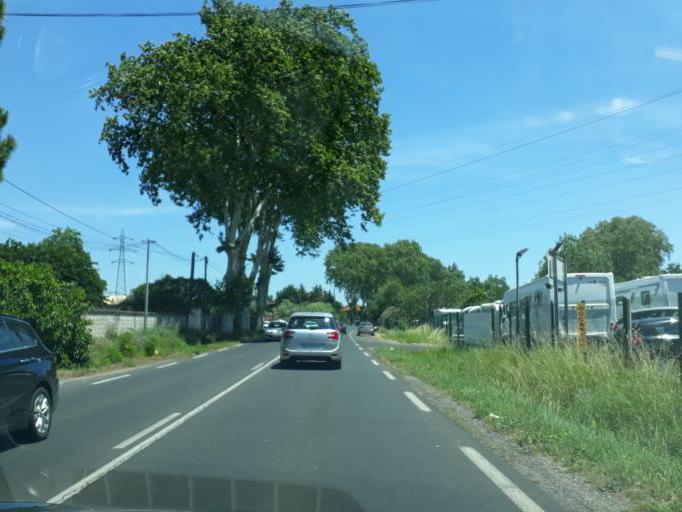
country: FR
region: Languedoc-Roussillon
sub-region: Departement de l'Herault
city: Villeneuve-les-Beziers
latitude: 43.3237
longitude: 3.2599
